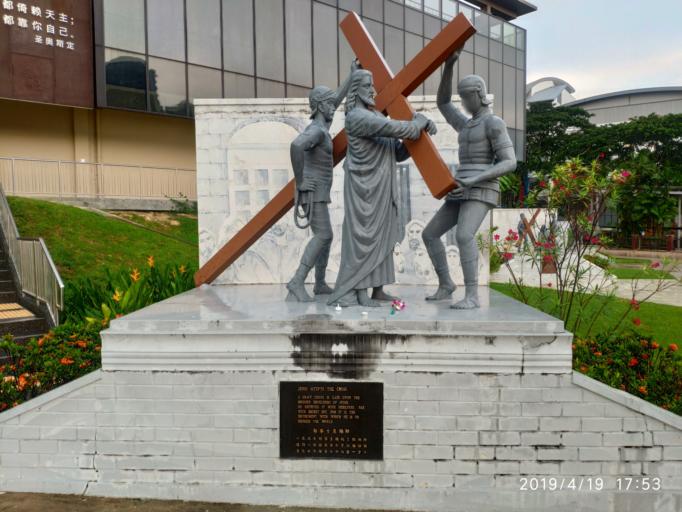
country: MY
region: Johor
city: Johor Bahru
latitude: 1.3672
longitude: 103.7666
